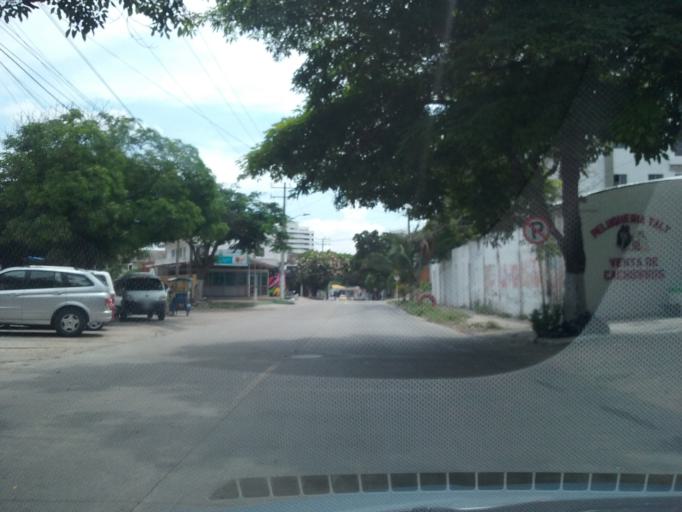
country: CO
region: Atlantico
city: Barranquilla
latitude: 11.0106
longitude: -74.8065
